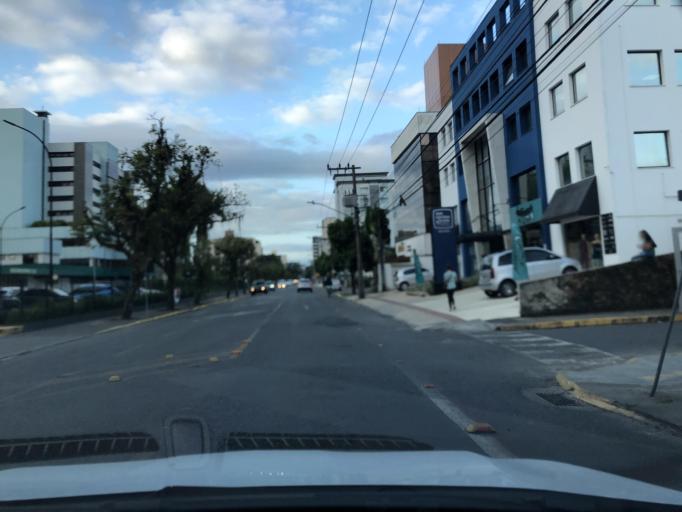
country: BR
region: Santa Catarina
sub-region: Joinville
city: Joinville
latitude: -26.2908
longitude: -48.8455
